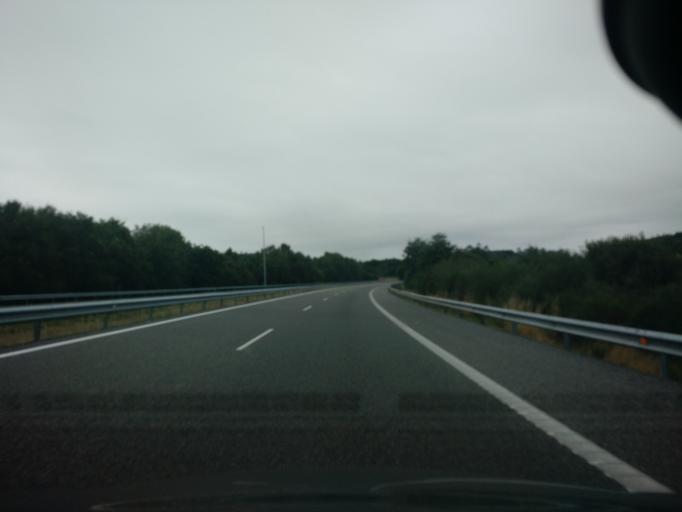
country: ES
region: Galicia
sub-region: Provincia da Coruna
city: Santiago de Compostela
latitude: 42.9135
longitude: -8.4776
